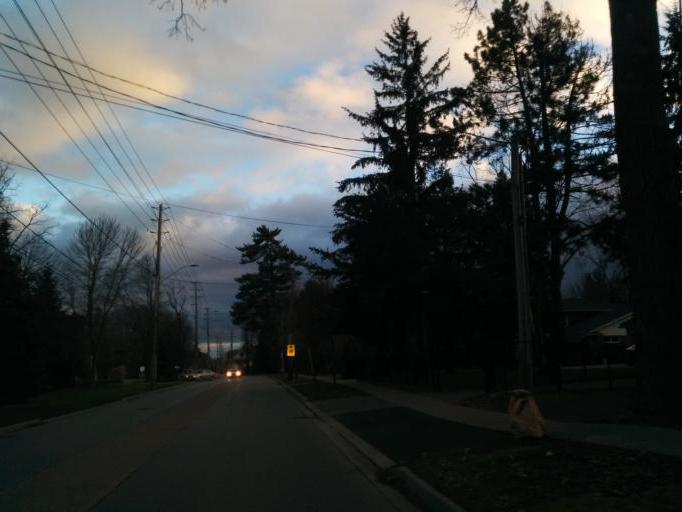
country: CA
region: Ontario
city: Mississauga
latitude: 43.5213
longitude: -79.6294
